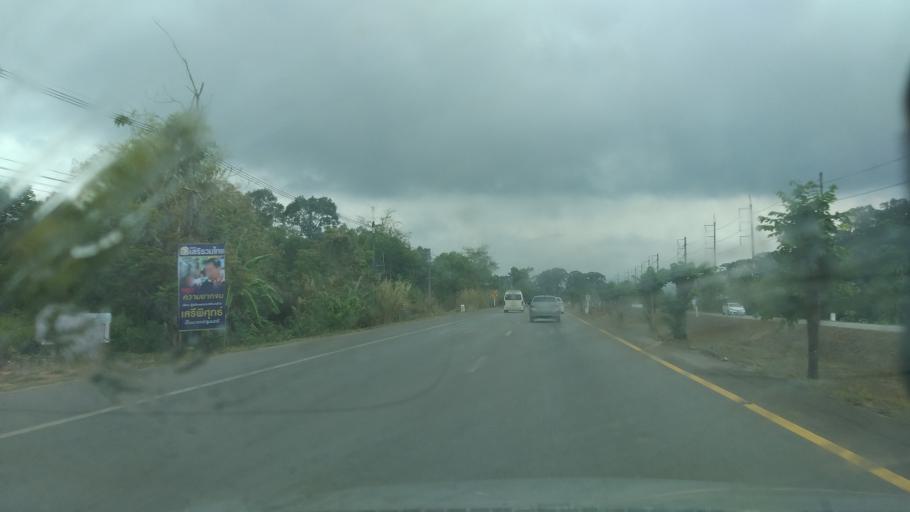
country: TH
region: Chanthaburi
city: Khlung
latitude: 12.4559
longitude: 102.2733
